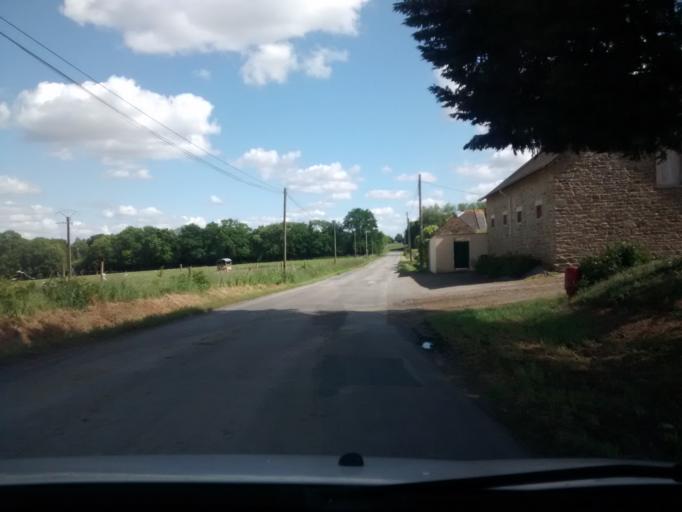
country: FR
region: Brittany
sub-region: Departement d'Ille-et-Vilaine
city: Cesson-Sevigne
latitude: 48.1418
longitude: -1.6046
